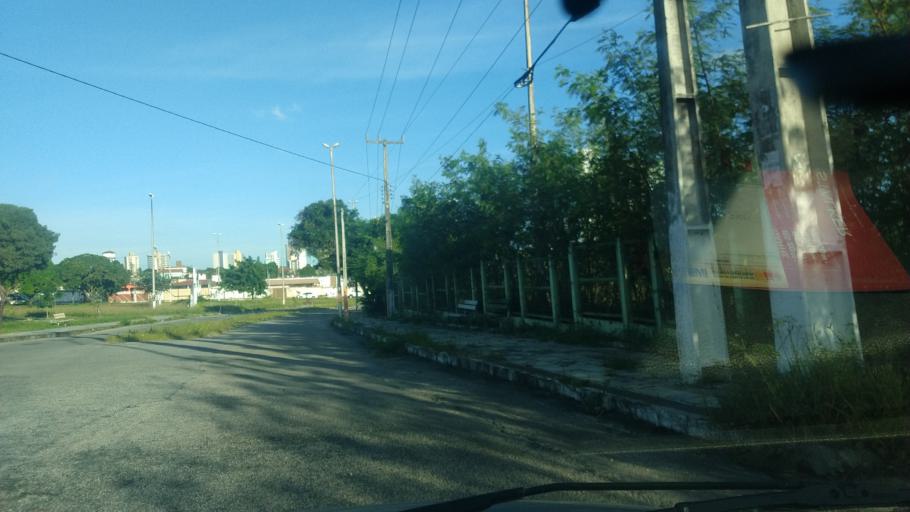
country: BR
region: Rio Grande do Norte
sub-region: Natal
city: Natal
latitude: -5.8753
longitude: -35.1862
